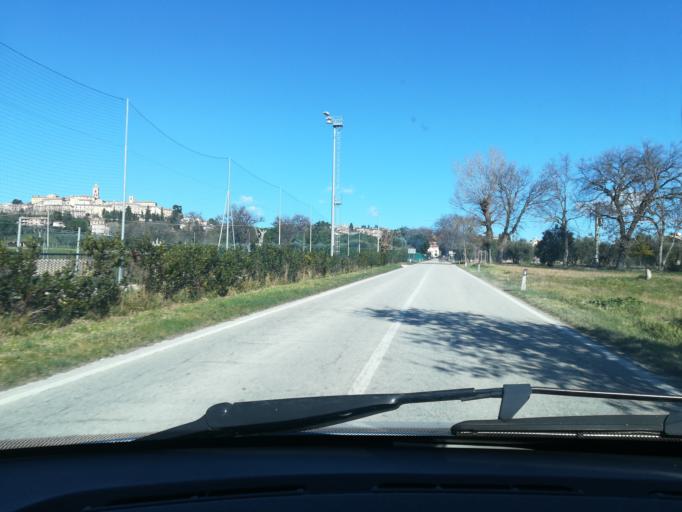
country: IT
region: The Marches
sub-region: Provincia di Macerata
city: Montecassiano
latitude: 43.3576
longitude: 13.4406
